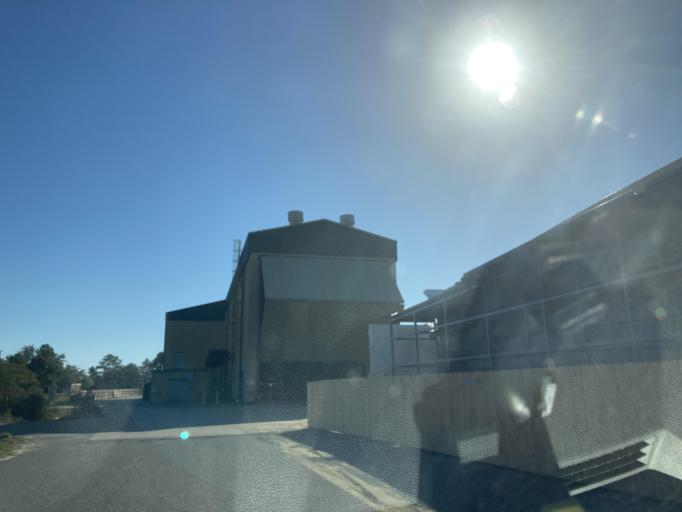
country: US
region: Mississippi
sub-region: Harrison County
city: West Gulfport
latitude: 30.4332
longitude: -89.0560
